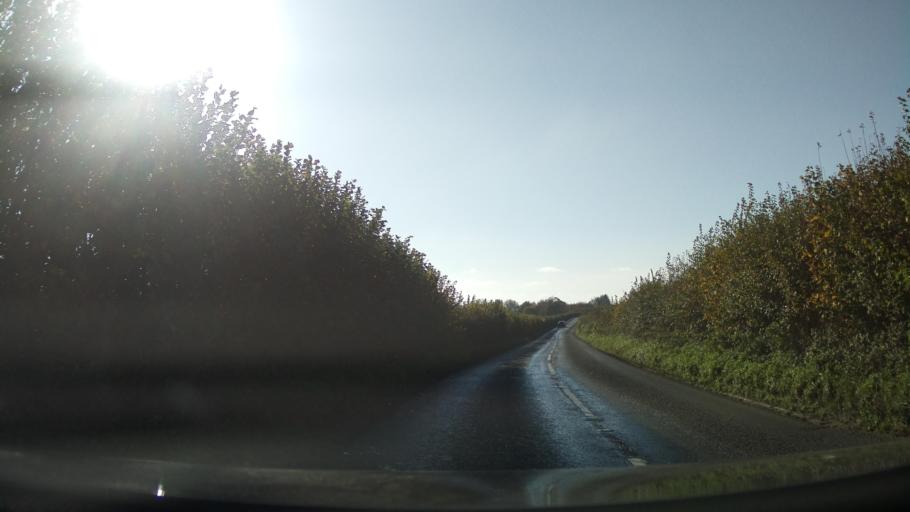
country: GB
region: England
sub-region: Somerset
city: Bruton
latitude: 51.1308
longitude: -2.4320
